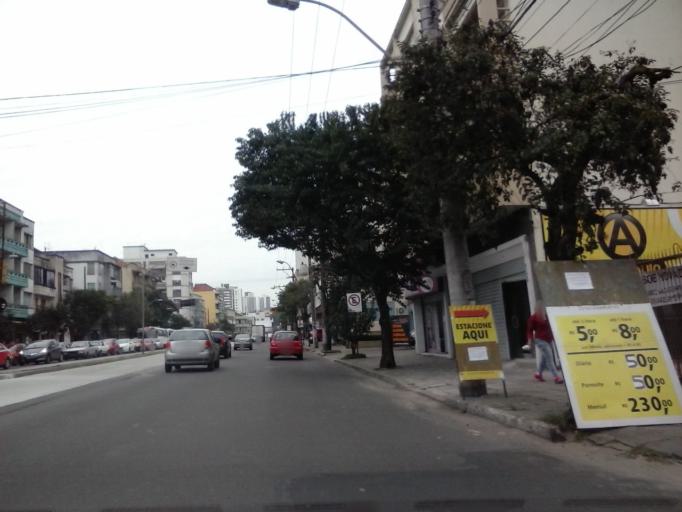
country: BR
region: Rio Grande do Sul
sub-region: Porto Alegre
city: Porto Alegre
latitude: -30.0392
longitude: -51.2010
